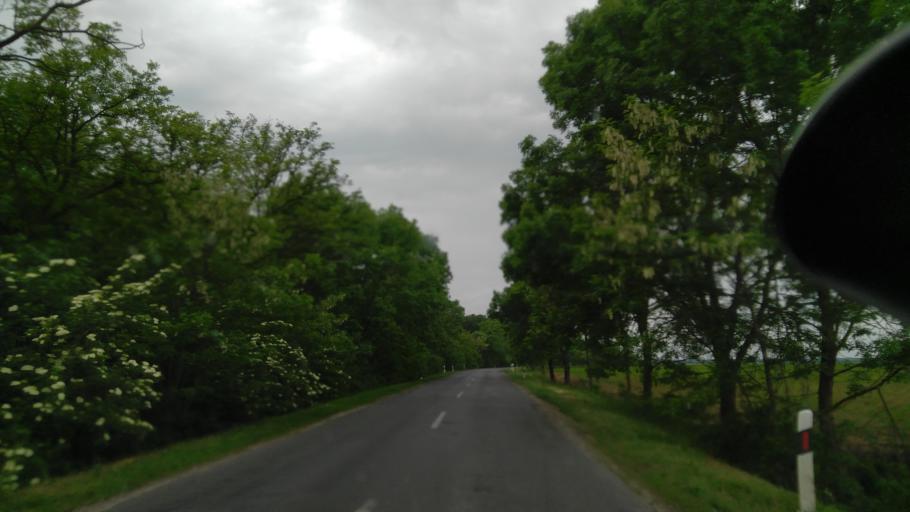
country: HU
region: Bekes
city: Doboz
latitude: 46.7235
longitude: 21.2998
